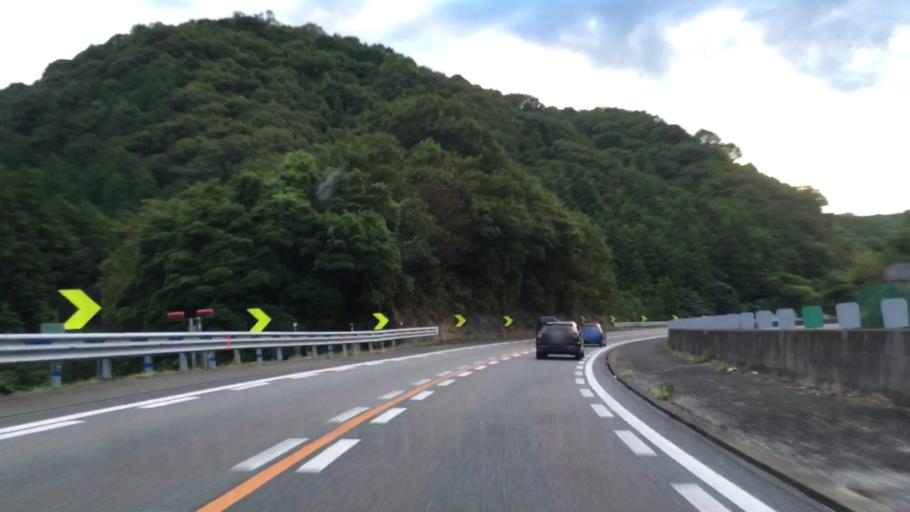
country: JP
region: Yamaguchi
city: Onoda
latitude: 34.1172
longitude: 131.1998
